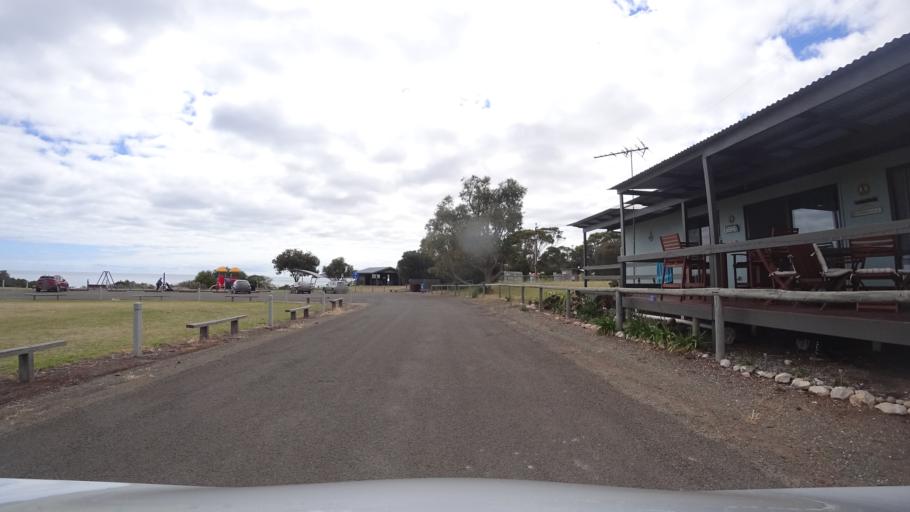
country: AU
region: South Australia
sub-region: Kangaroo Island
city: Kingscote
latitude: -35.5941
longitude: 137.5062
